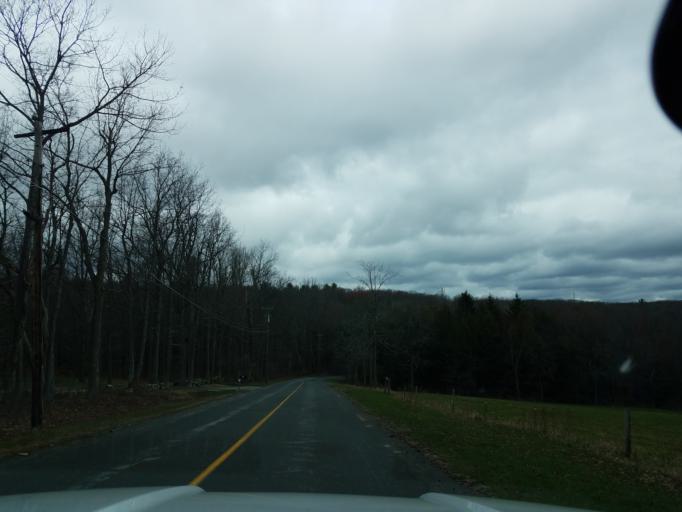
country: US
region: Connecticut
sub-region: Litchfield County
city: Litchfield
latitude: 41.7907
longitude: -73.1794
